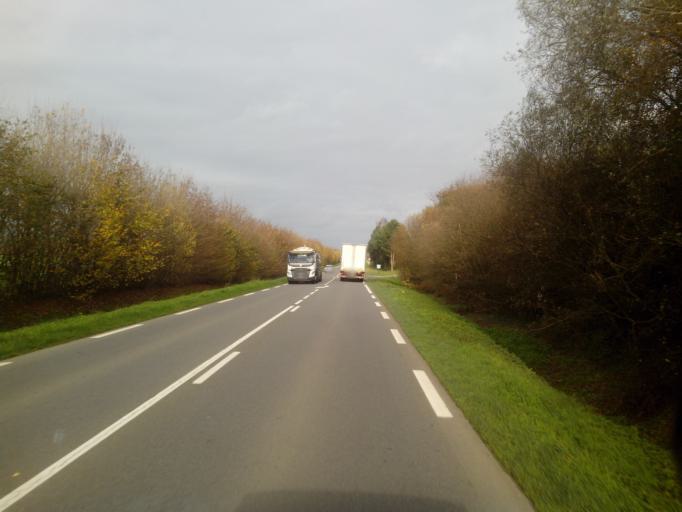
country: FR
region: Brittany
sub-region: Departement d'Ille-et-Vilaine
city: Gael
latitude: 48.1569
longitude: -2.2119
